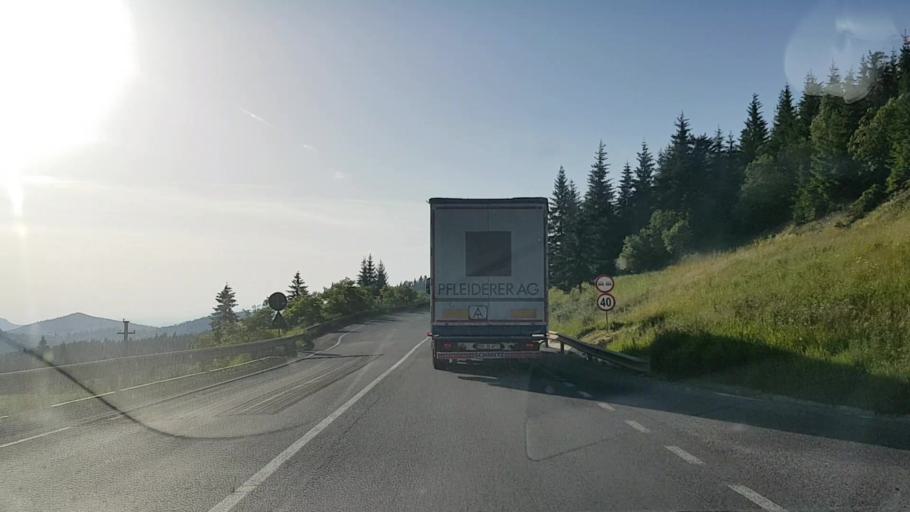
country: RO
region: Bistrita-Nasaud
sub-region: Comuna Lunca Ilvei
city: Lunca Ilvei
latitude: 47.2635
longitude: 25.0212
